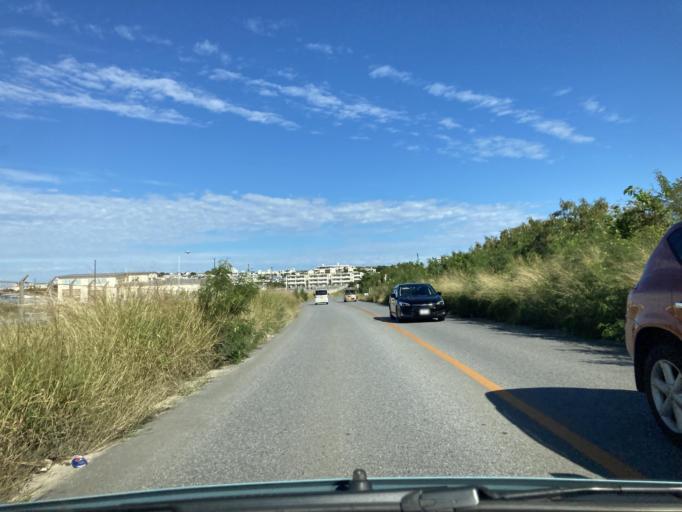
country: JP
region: Okinawa
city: Okinawa
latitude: 26.3758
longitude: 127.7458
